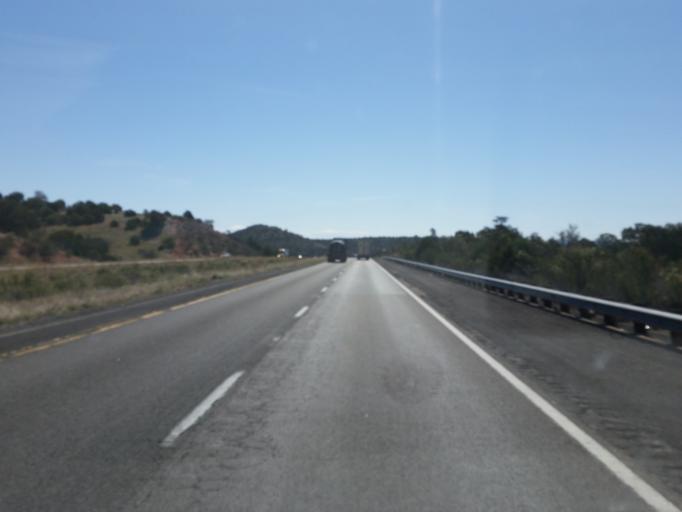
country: US
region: Arizona
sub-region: Mohave County
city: Peach Springs
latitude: 35.2921
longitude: -113.0425
